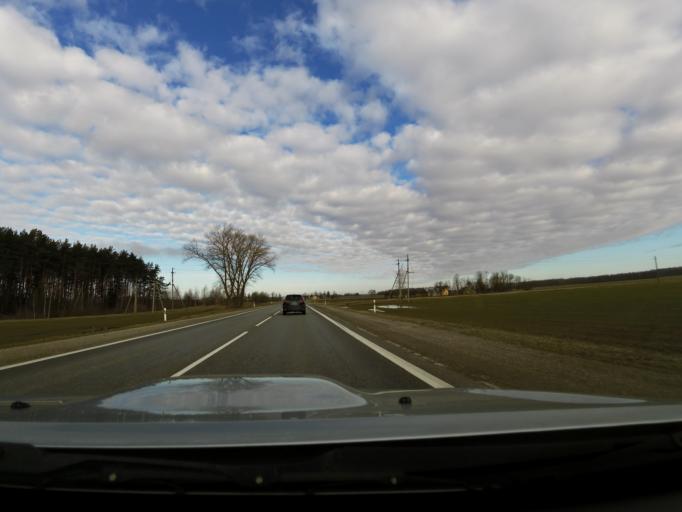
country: LT
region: Siauliu apskritis
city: Pakruojis
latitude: 55.7695
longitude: 24.0634
